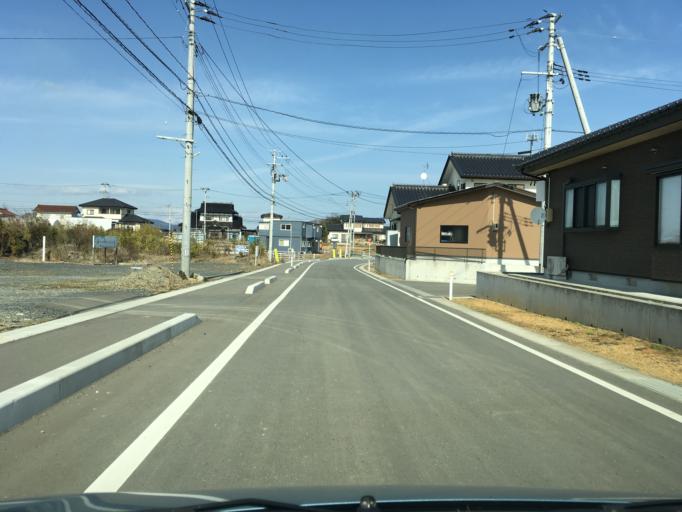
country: JP
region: Iwate
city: Ofunato
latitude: 38.8303
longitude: 141.5857
